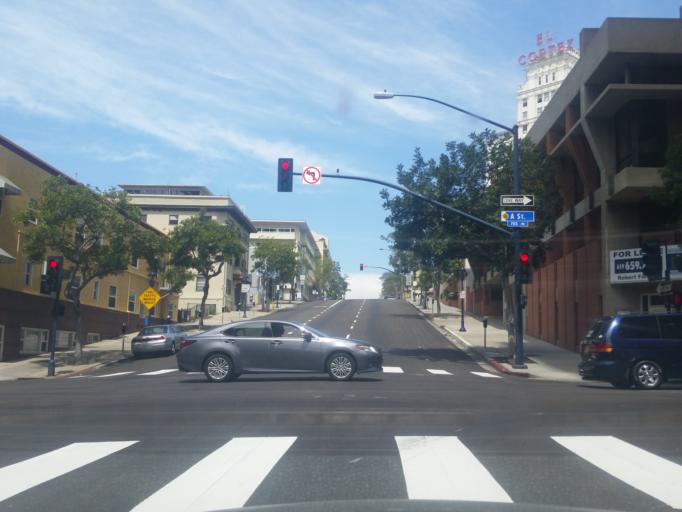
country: US
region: California
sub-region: San Diego County
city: San Diego
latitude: 32.7187
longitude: -117.1583
